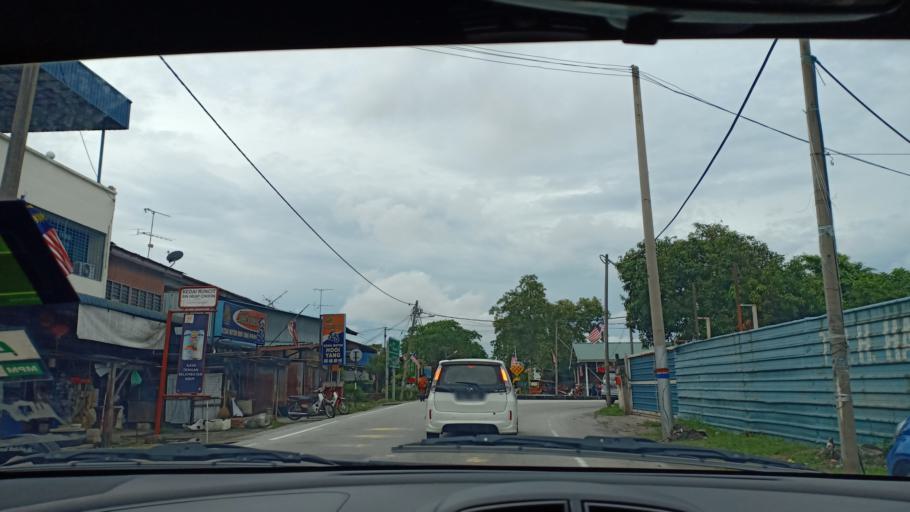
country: MY
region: Penang
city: Bukit Mertajam
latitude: 5.4038
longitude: 100.4633
